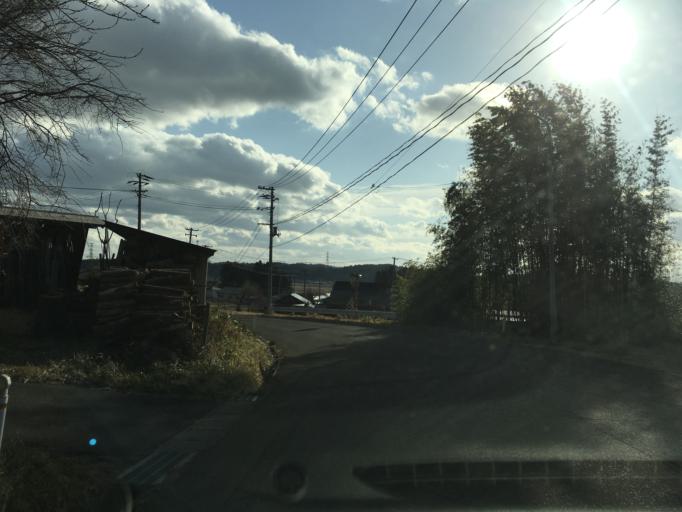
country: JP
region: Iwate
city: Ichinoseki
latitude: 38.8100
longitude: 140.9952
